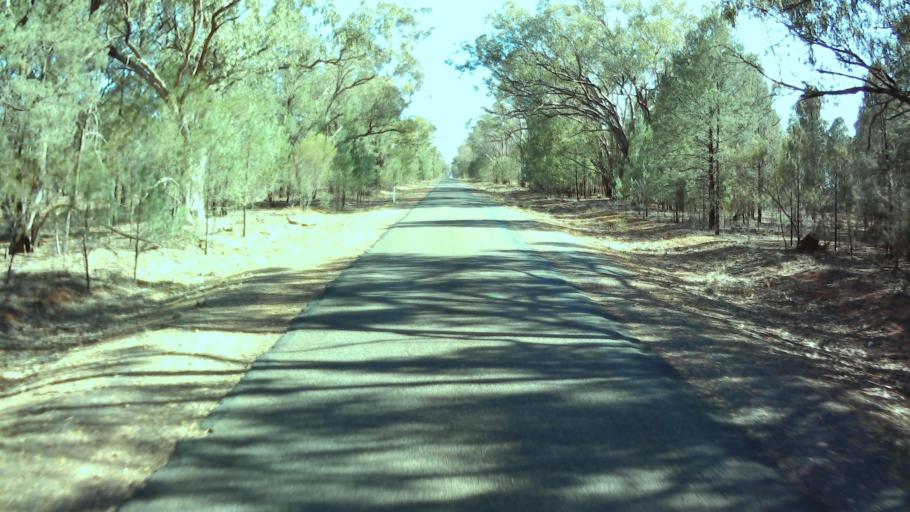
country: AU
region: New South Wales
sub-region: Weddin
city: Grenfell
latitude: -33.8109
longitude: 147.9540
